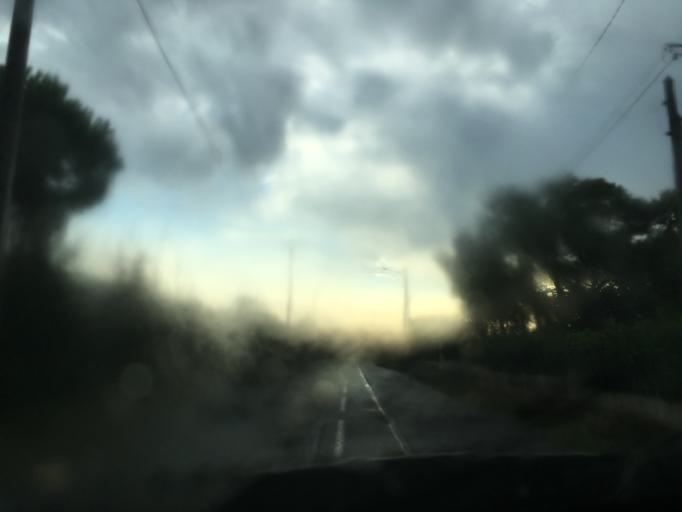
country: FR
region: Midi-Pyrenees
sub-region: Departement de la Haute-Garonne
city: Plaisance-du-Touch
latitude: 43.5598
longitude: 1.3218
